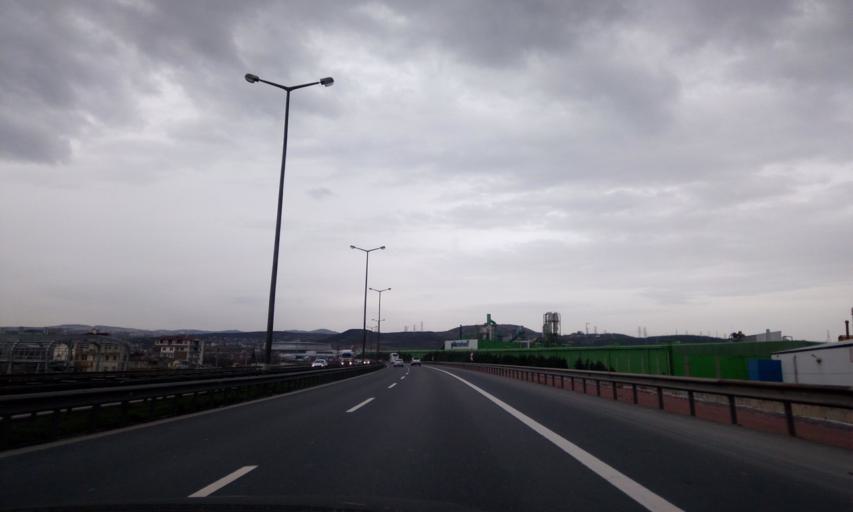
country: TR
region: Kocaeli
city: Kosekoy
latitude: 40.7584
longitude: 30.0364
